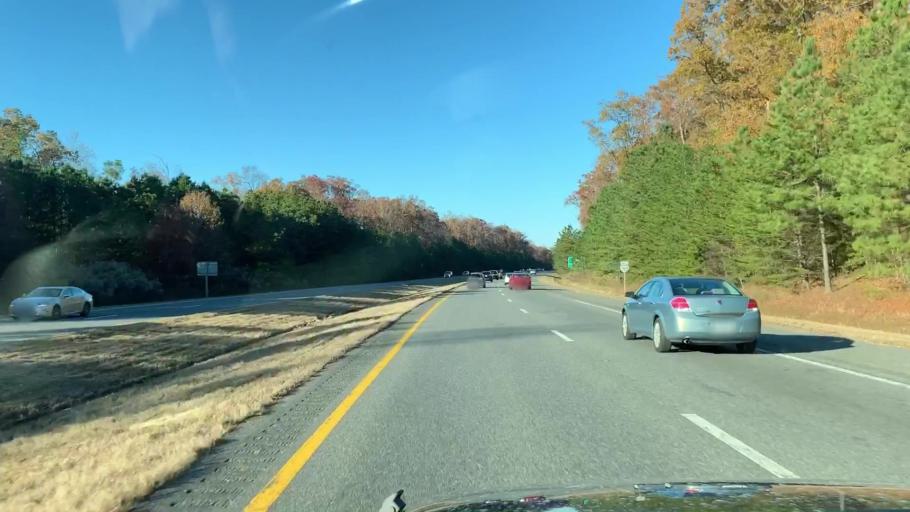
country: US
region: Virginia
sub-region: James City County
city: Williamsburg
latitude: 37.2798
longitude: -76.7533
